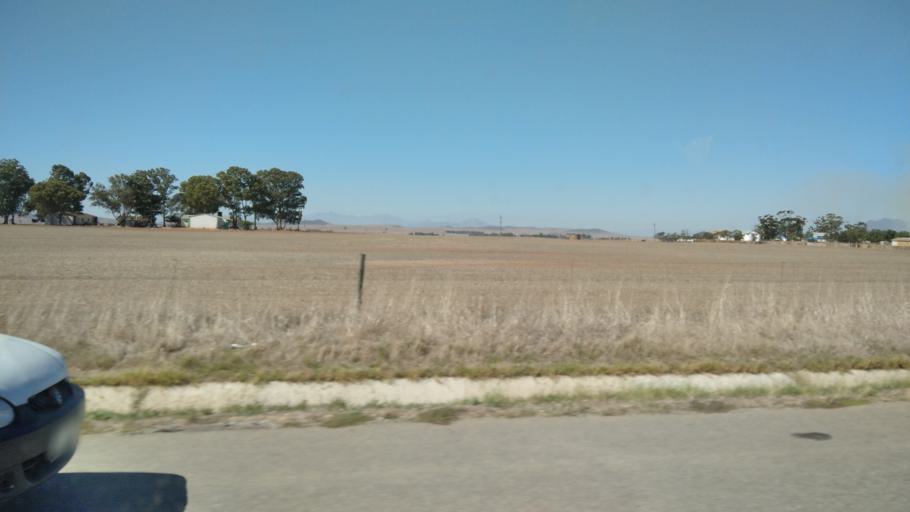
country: ZA
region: Western Cape
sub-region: West Coast District Municipality
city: Moorreesburg
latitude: -33.2836
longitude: 18.6046
